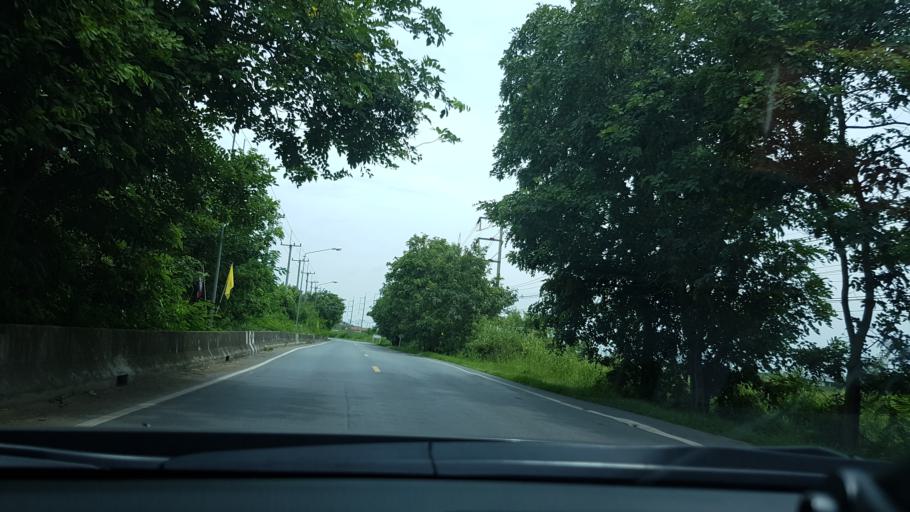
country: TH
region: Pathum Thani
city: Sam Khok
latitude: 14.1409
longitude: 100.5292
